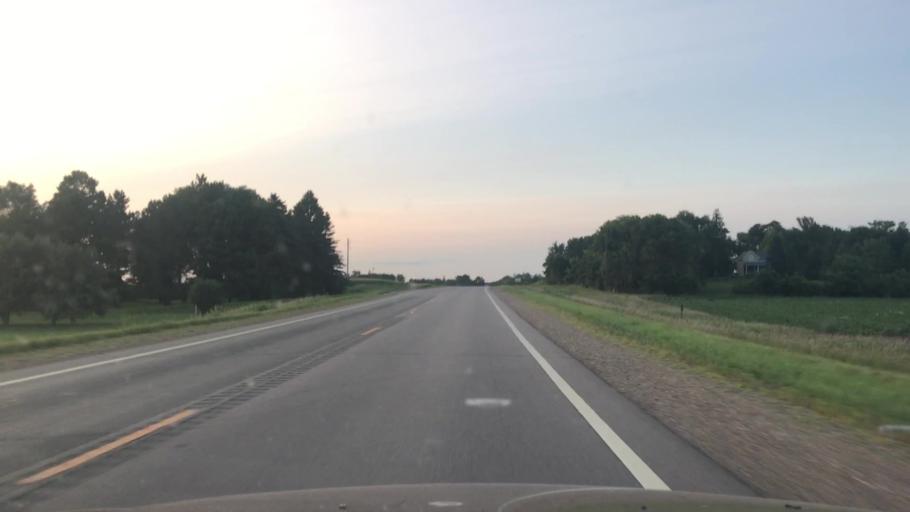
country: US
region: Minnesota
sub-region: Redwood County
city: Redwood Falls
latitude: 44.5164
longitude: -95.1181
